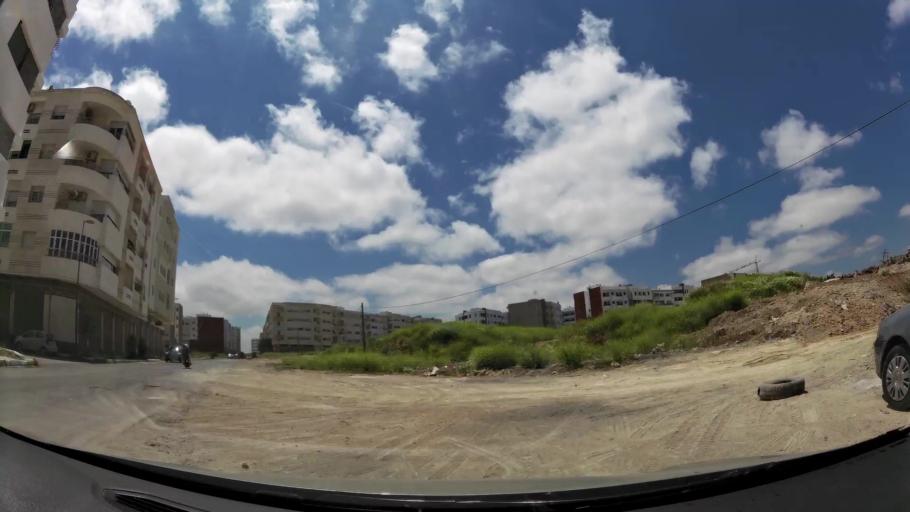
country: MA
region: Fes-Boulemane
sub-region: Fes
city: Fes
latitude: 34.0402
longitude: -5.0147
